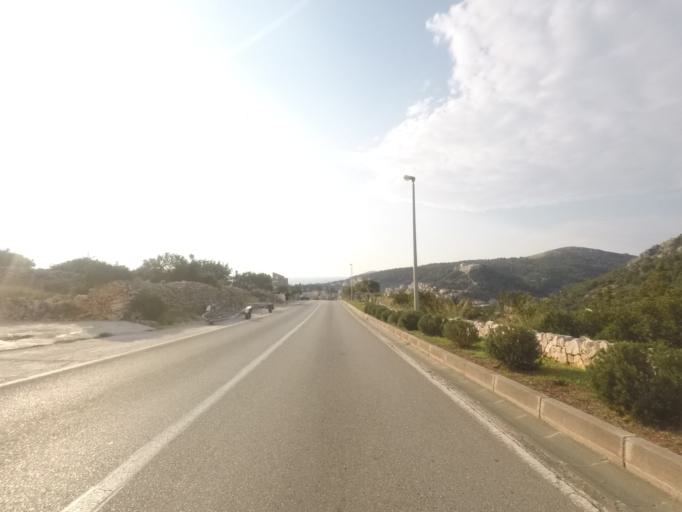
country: HR
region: Splitsko-Dalmatinska
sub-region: Grad Hvar
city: Hvar
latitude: 43.1695
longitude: 16.4513
